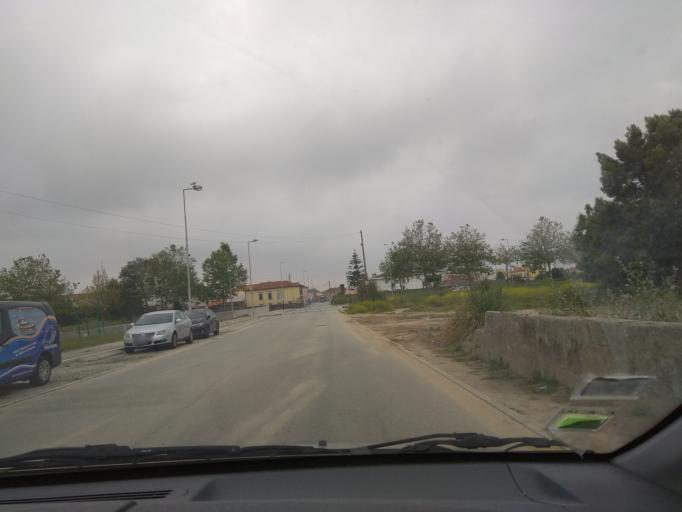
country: PT
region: Porto
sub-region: Matosinhos
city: Guifoes
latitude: 41.1984
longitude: -8.6651
